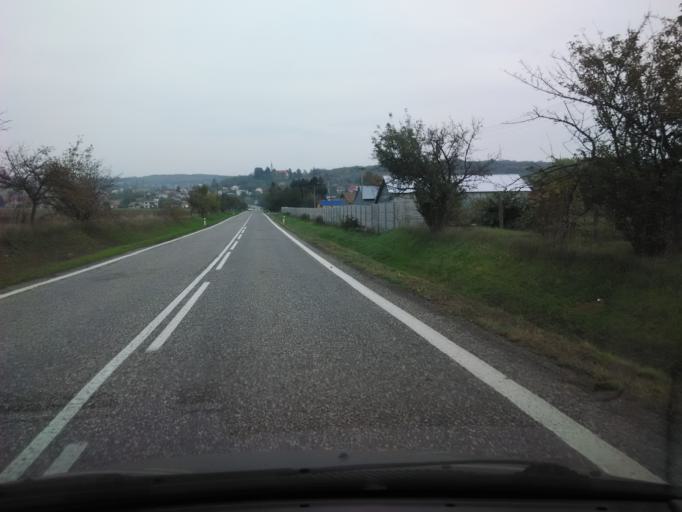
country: SK
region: Nitriansky
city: Svodin
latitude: 48.0347
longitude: 18.4586
